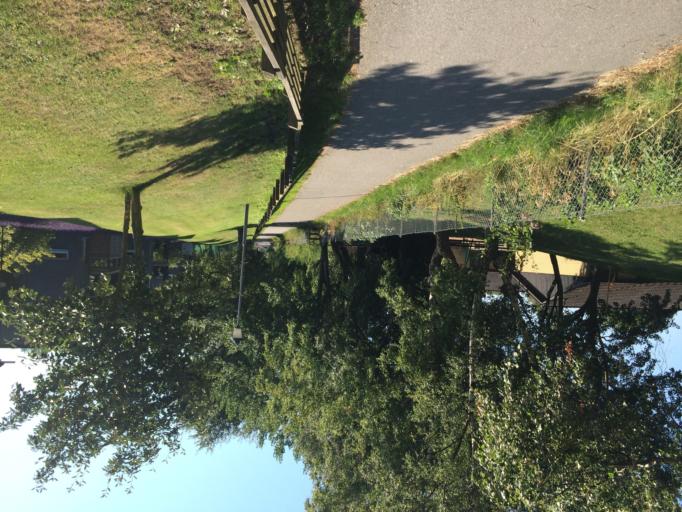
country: SE
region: Skane
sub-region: Vellinge Kommun
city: Skanor med Falsterbo
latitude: 55.4049
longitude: 12.8430
